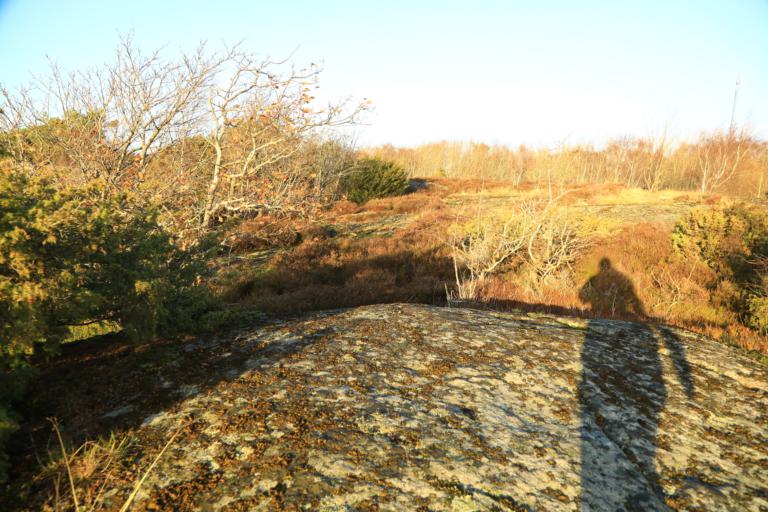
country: SE
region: Halland
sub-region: Varbergs Kommun
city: Varberg
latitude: 57.1716
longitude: 12.2306
